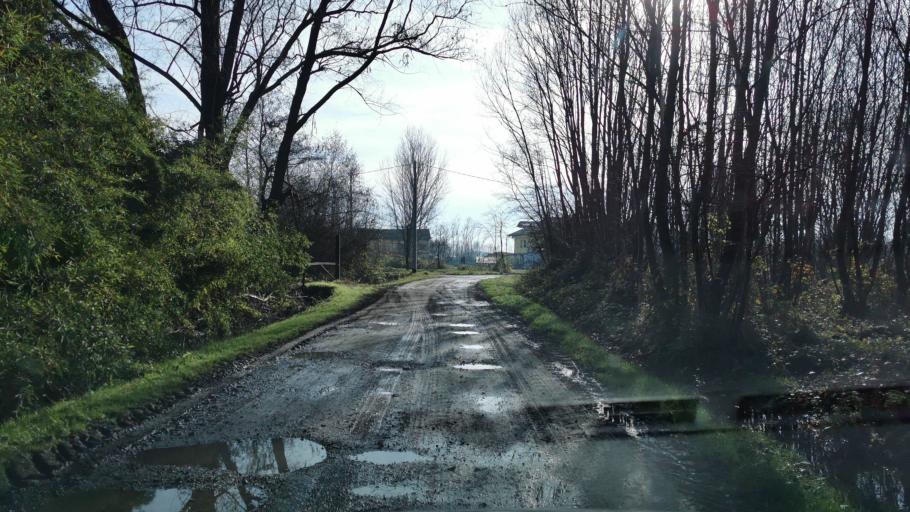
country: IT
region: Piedmont
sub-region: Provincia di Torino
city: Bosconero
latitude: 45.2716
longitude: 7.7763
